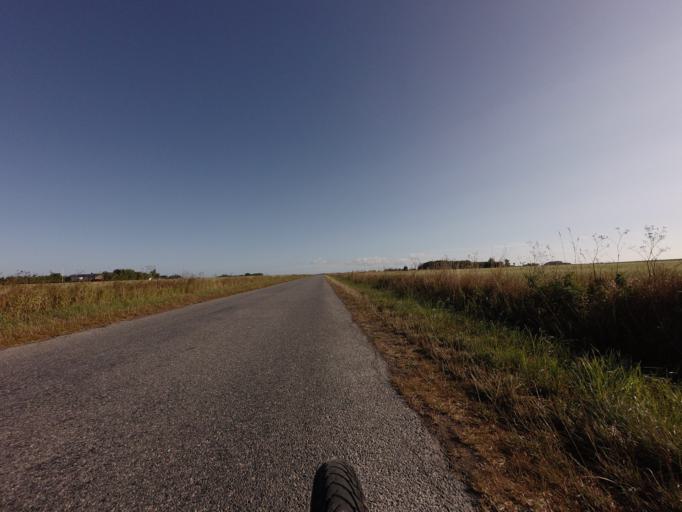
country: DK
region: North Denmark
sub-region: Hjorring Kommune
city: Vra
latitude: 57.3905
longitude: 9.9267
